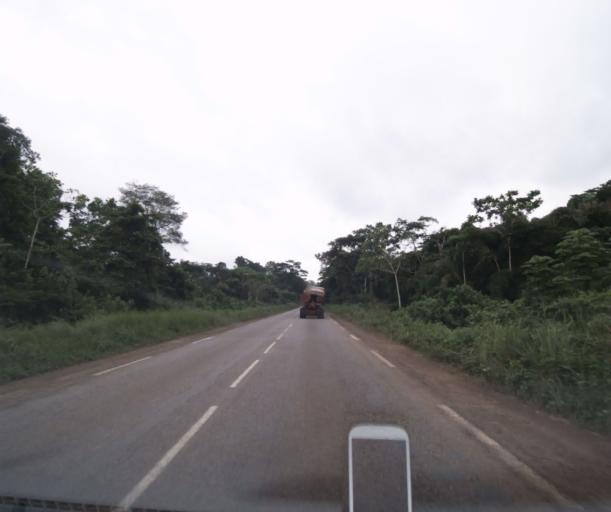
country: CM
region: Littoral
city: Edea
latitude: 3.8118
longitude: 10.3026
